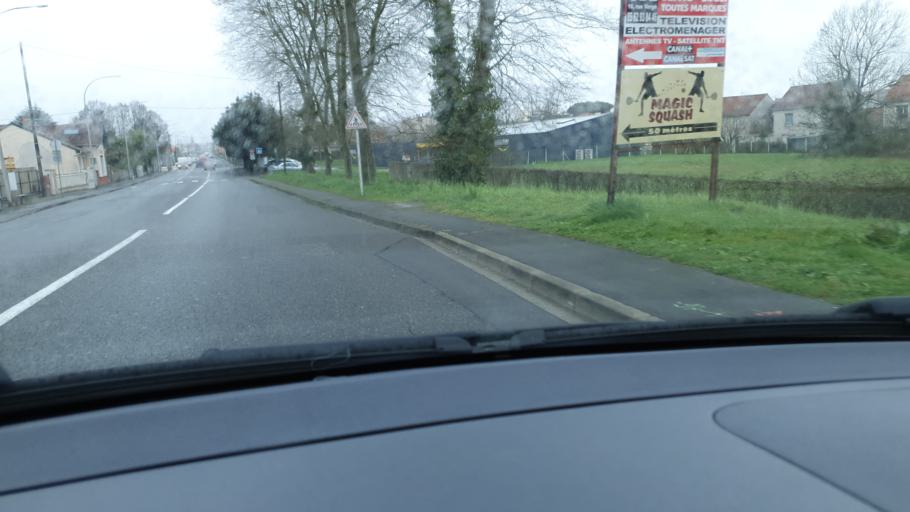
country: FR
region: Midi-Pyrenees
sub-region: Departement des Hautes-Pyrenees
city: Tarbes
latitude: 43.2372
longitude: 0.0488
